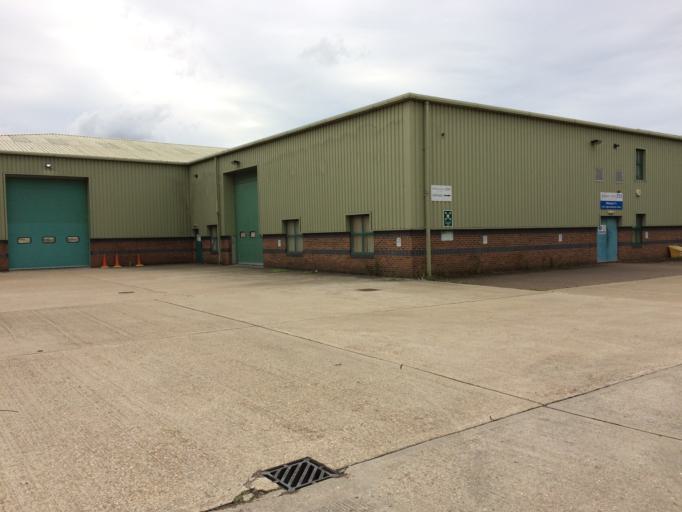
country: GB
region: England
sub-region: East Sussex
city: Hailsham
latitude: 50.8604
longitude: 0.2465
